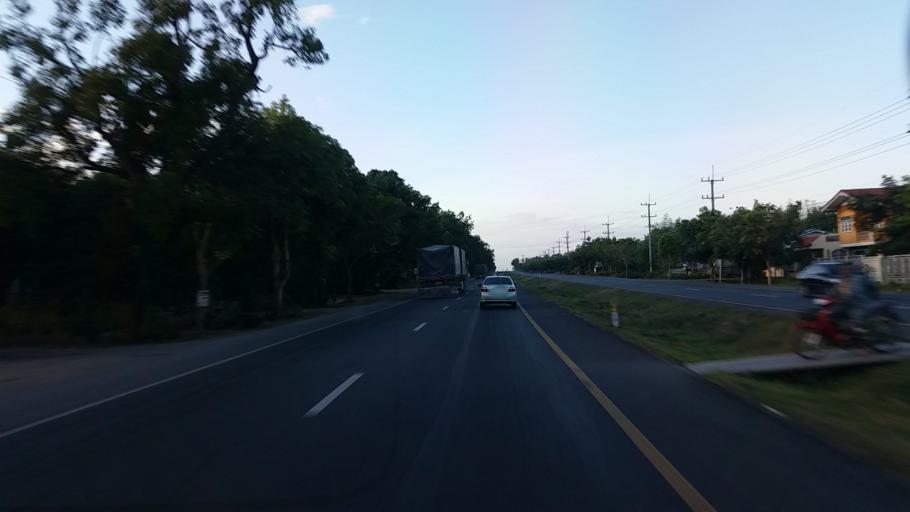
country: TH
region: Lop Buri
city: Chai Badan
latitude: 15.1642
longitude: 101.0616
